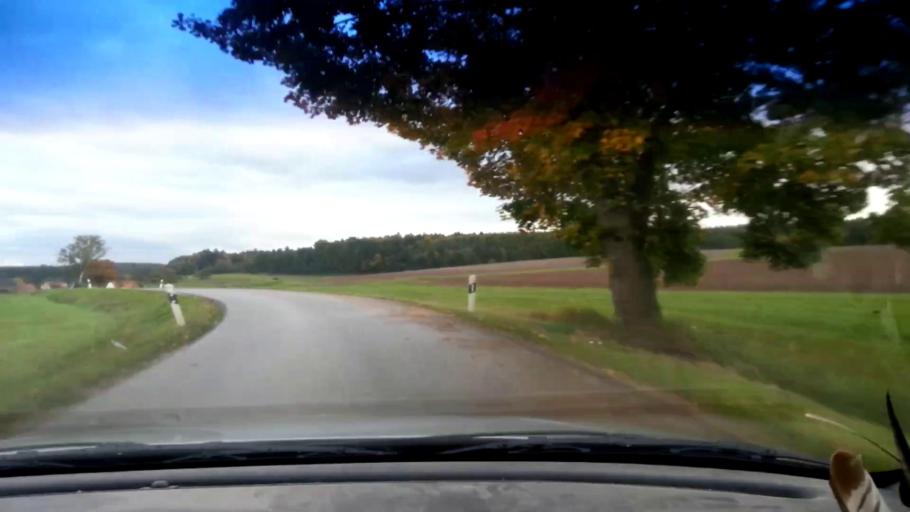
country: DE
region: Bavaria
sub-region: Upper Franconia
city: Burgebrach
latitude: 49.8105
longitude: 10.6926
